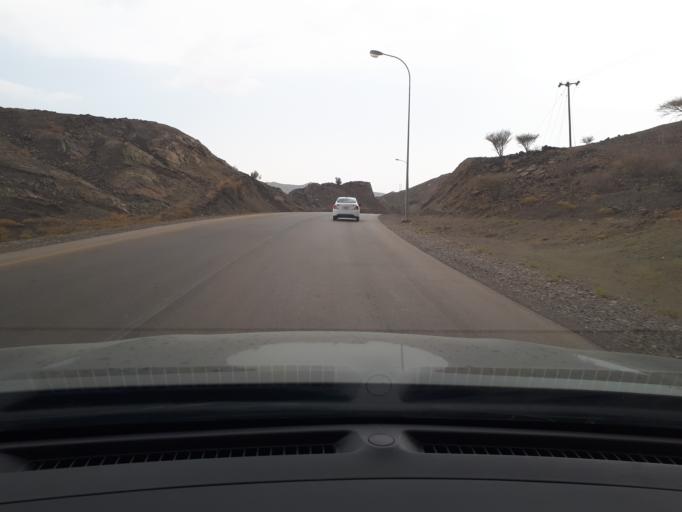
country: OM
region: Ash Sharqiyah
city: Badiyah
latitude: 22.5529
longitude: 59.0040
